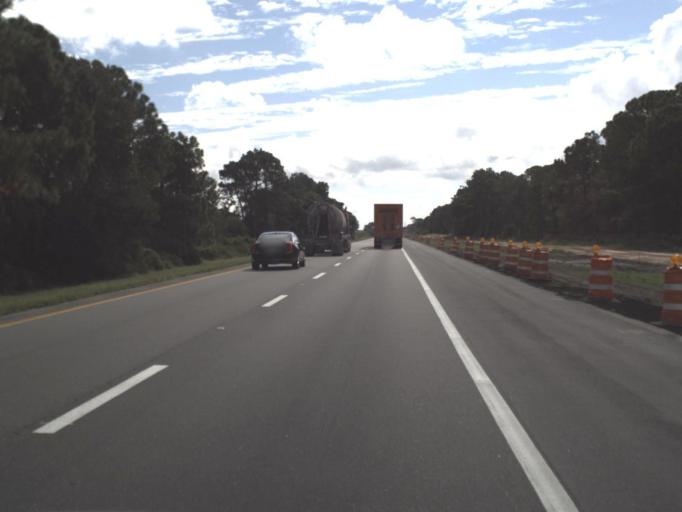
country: US
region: Florida
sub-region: Sarasota County
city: Warm Mineral Springs
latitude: 27.0996
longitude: -82.2467
